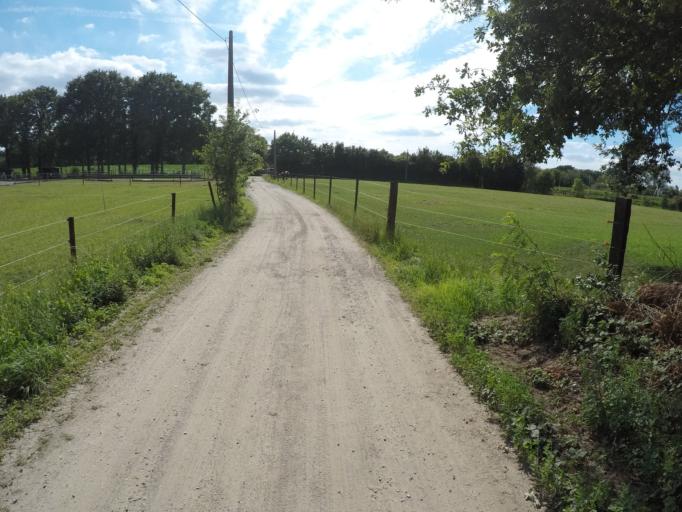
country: BE
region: Flanders
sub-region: Provincie Antwerpen
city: Nijlen
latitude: 51.1476
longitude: 4.6518
